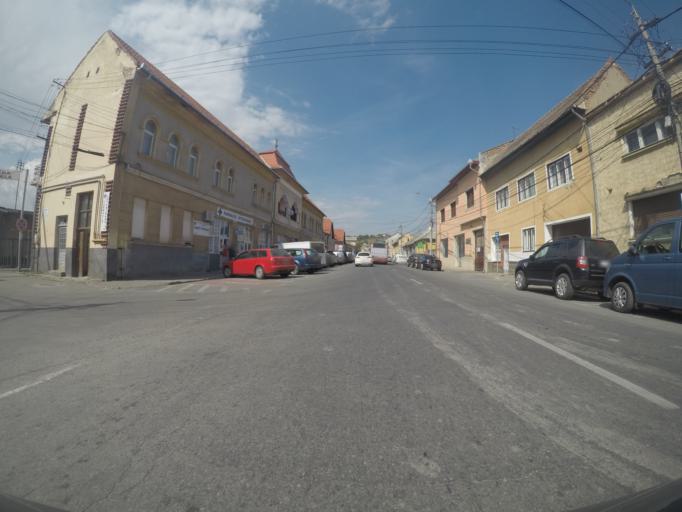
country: RO
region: Cluj
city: Turda
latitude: 46.5715
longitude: 23.7878
